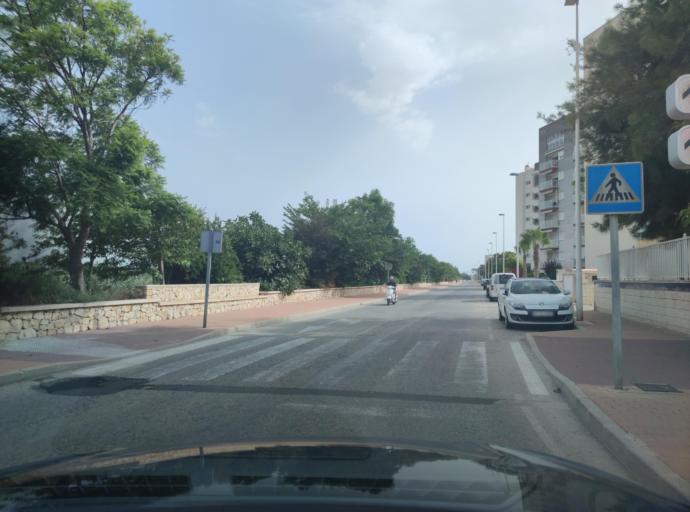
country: ES
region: Valencia
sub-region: Provincia de Alicante
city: Guardamar del Segura
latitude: 38.1031
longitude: -0.6559
